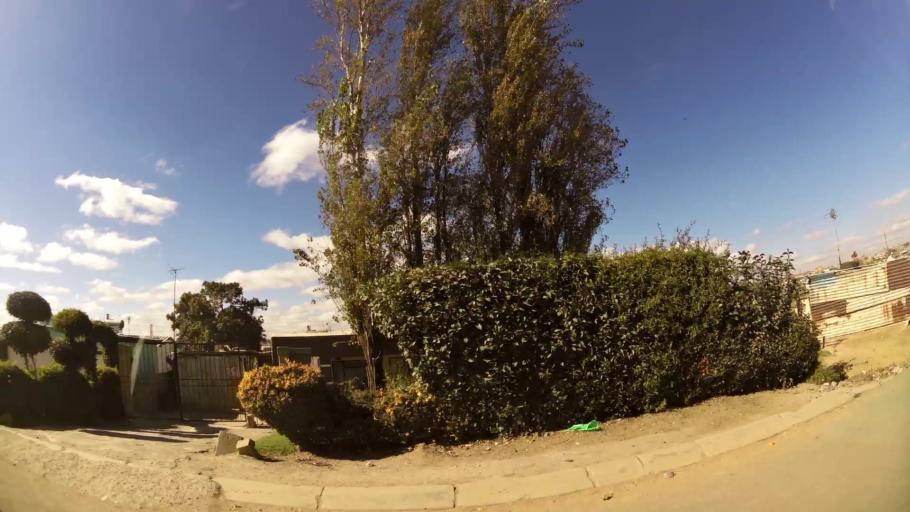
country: ZA
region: Gauteng
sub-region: Ekurhuleni Metropolitan Municipality
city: Tembisa
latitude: -26.0345
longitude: 28.1875
